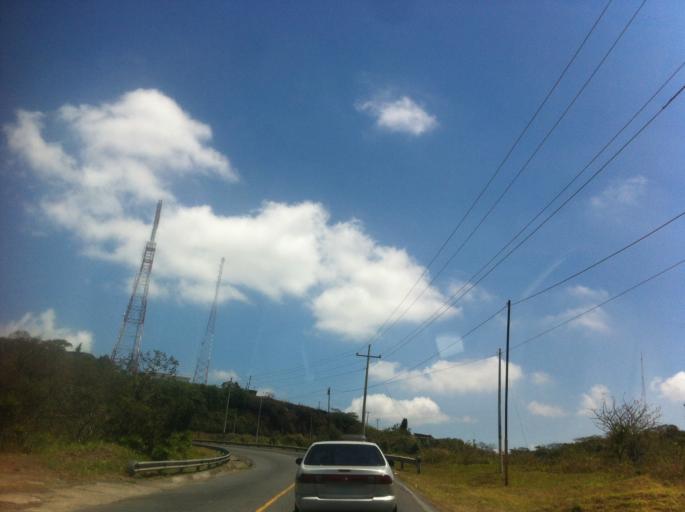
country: NI
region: Managua
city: El Crucero
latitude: 11.9963
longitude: -86.3114
